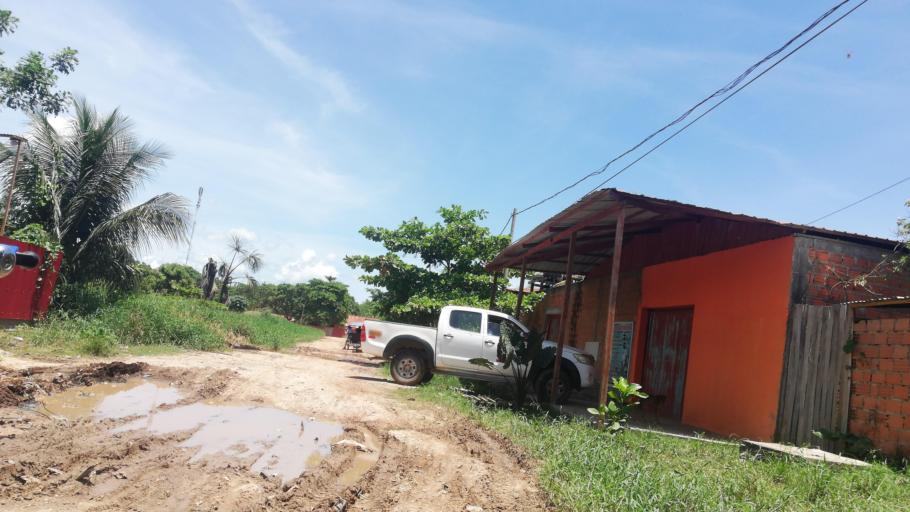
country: PE
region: Ucayali
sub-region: Provincia de Coronel Portillo
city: Puerto Callao
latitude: -8.3598
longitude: -74.5917
